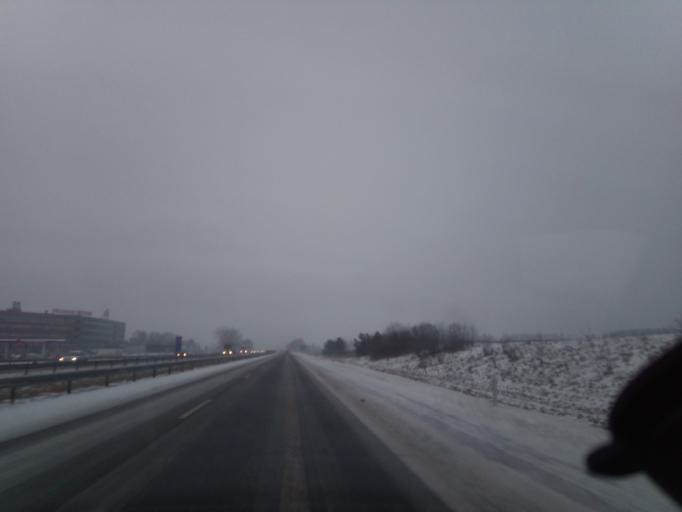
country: LT
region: Vilnius County
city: Pasilaiciai
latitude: 54.7695
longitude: 25.1933
